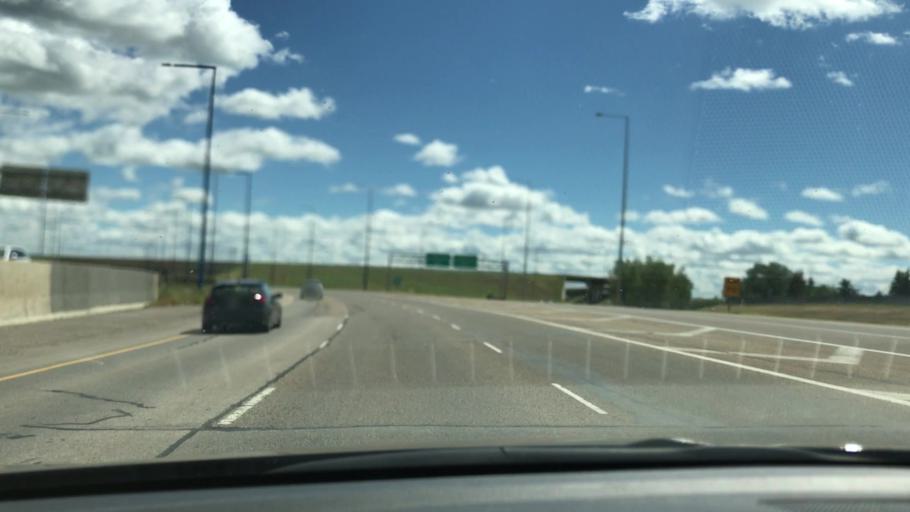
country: CA
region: Alberta
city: Edmonton
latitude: 53.4426
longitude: -113.4930
